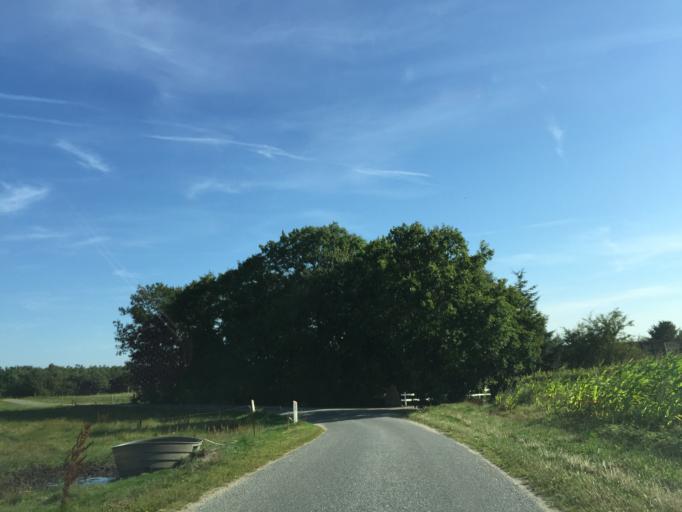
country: DK
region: Central Jutland
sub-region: Viborg Kommune
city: Bjerringbro
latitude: 56.2680
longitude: 9.7142
